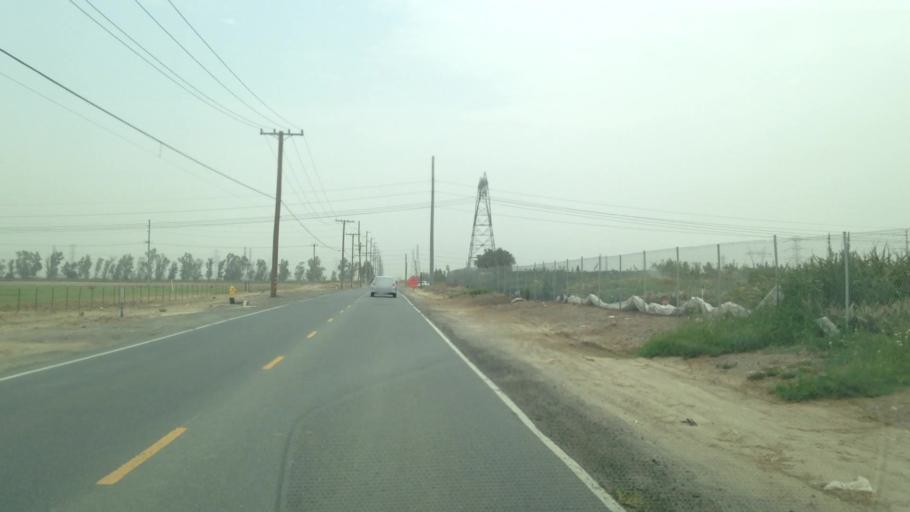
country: US
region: California
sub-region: Riverside County
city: Mira Loma
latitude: 34.0146
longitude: -117.5758
